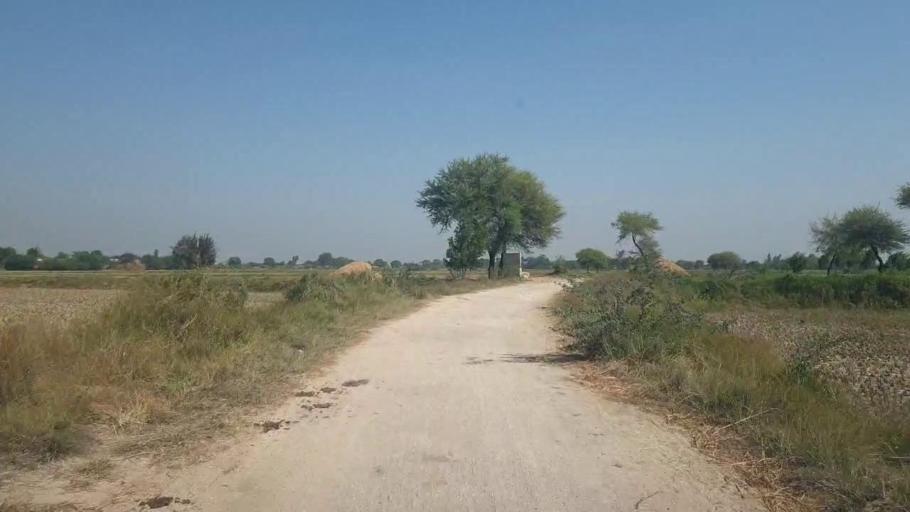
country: PK
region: Sindh
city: Badin
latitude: 24.6803
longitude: 68.8619
